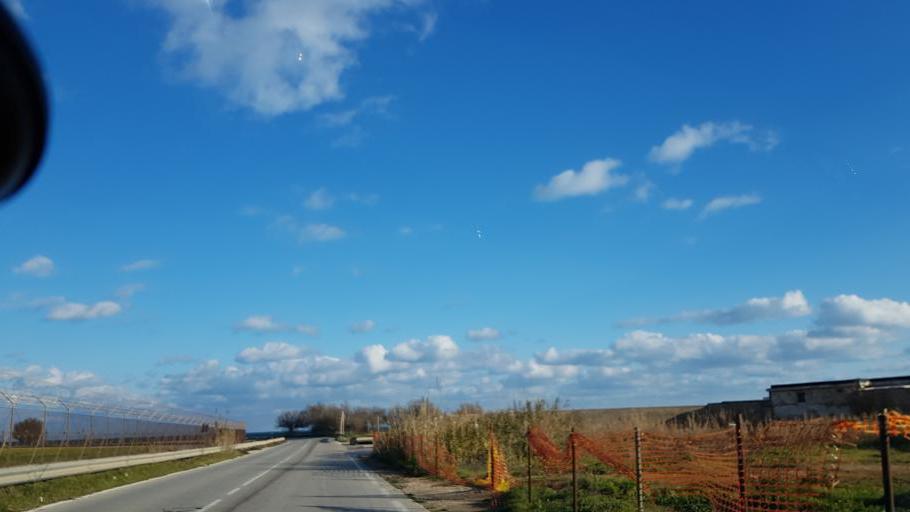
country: IT
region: Apulia
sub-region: Provincia di Brindisi
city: Materdomini
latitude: 40.6615
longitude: 17.9571
